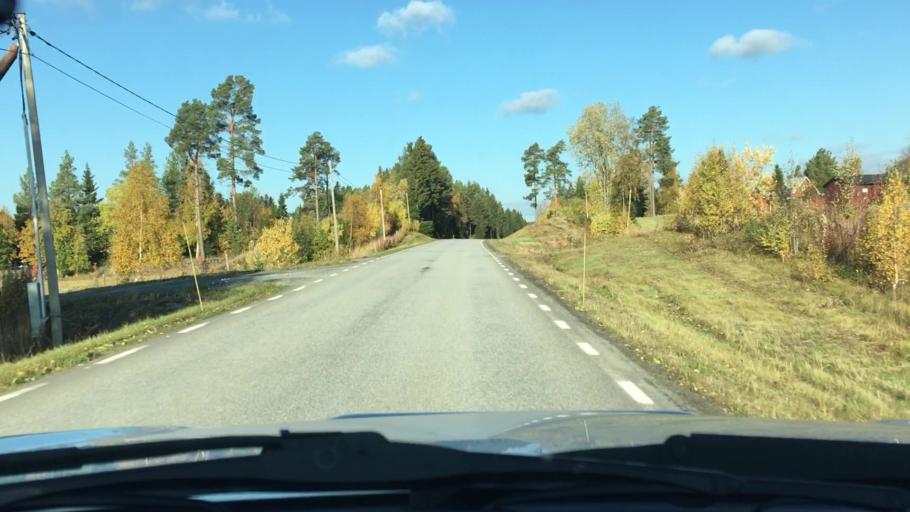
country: SE
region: Jaemtland
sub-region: Krokoms Kommun
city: Krokom
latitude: 63.3063
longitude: 14.2035
